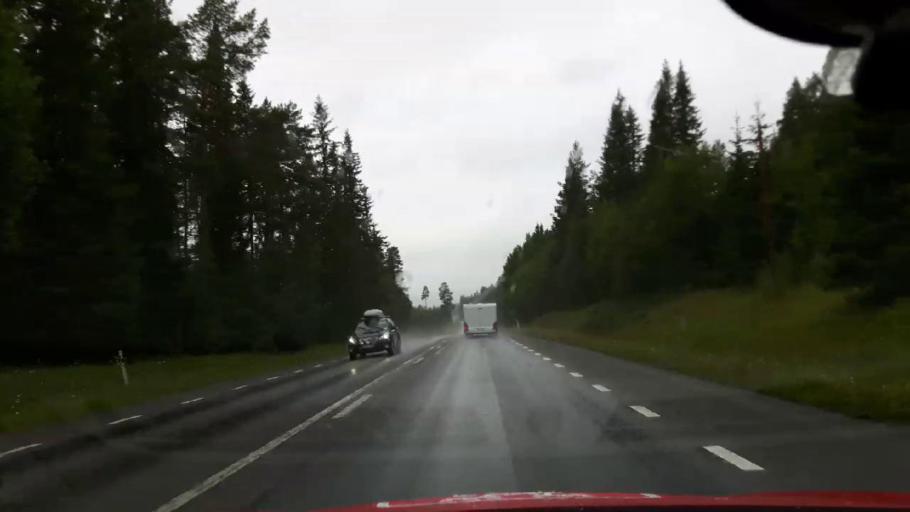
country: SE
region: Jaemtland
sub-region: Are Kommun
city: Jarpen
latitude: 63.3378
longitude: 13.4988
